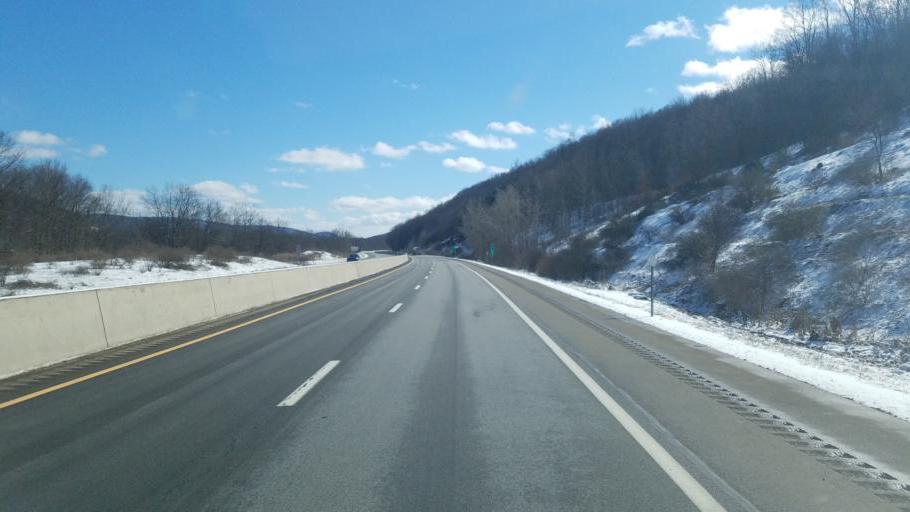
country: US
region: New York
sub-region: Cattaraugus County
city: Salamanca
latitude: 42.1263
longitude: -78.6664
